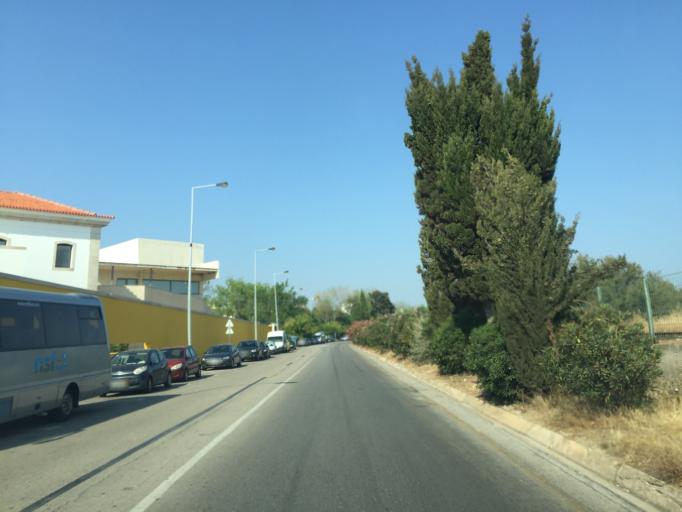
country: PT
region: Faro
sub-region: Faro
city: Faro
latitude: 37.0117
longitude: -7.9308
